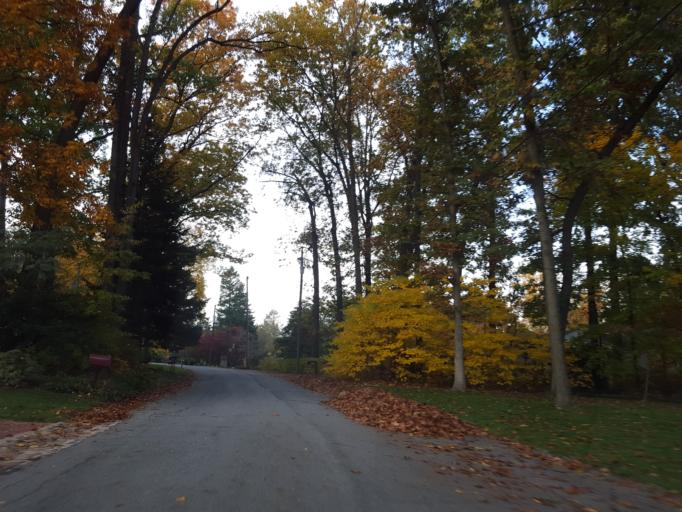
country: US
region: Pennsylvania
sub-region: York County
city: Stonybrook
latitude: 39.9752
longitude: -76.6327
